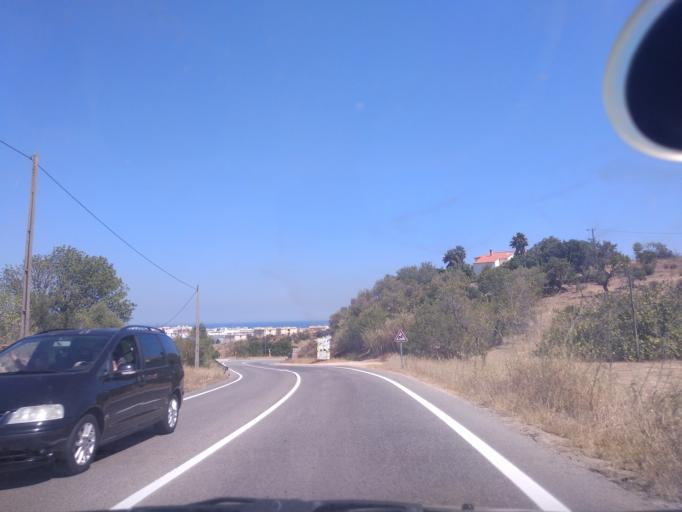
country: PT
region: Faro
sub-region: Lagos
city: Lagos
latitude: 37.1163
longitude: -8.6880
